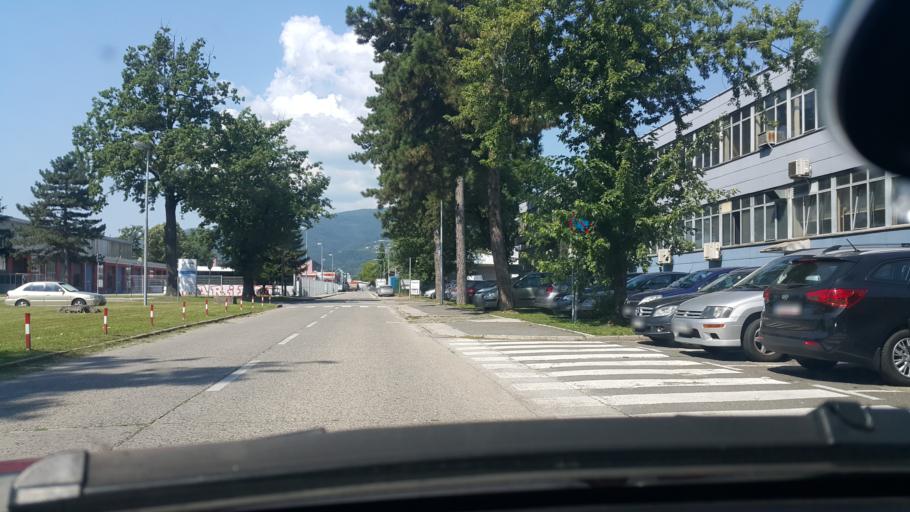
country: SI
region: Hoce-Slivnica
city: Spodnje Hoce
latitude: 46.5269
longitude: 15.6646
